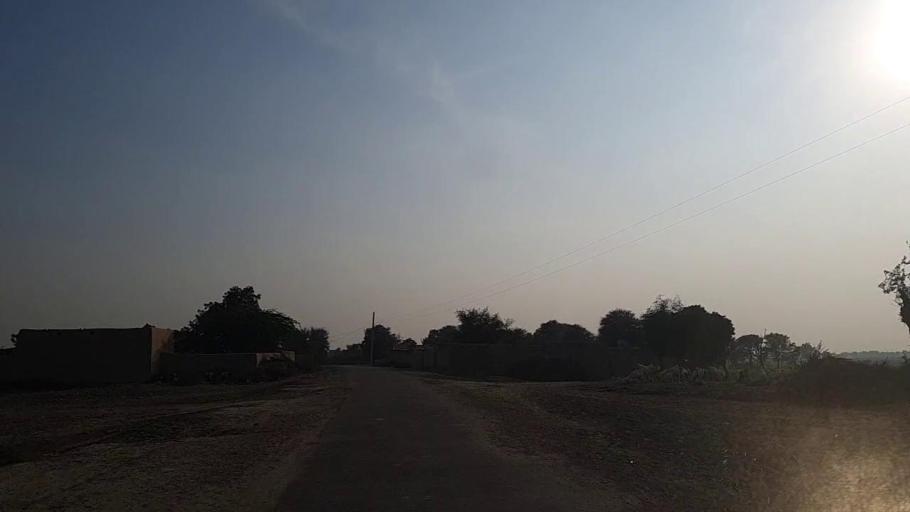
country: PK
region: Sindh
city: Jam Sahib
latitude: 26.4473
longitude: 68.5834
